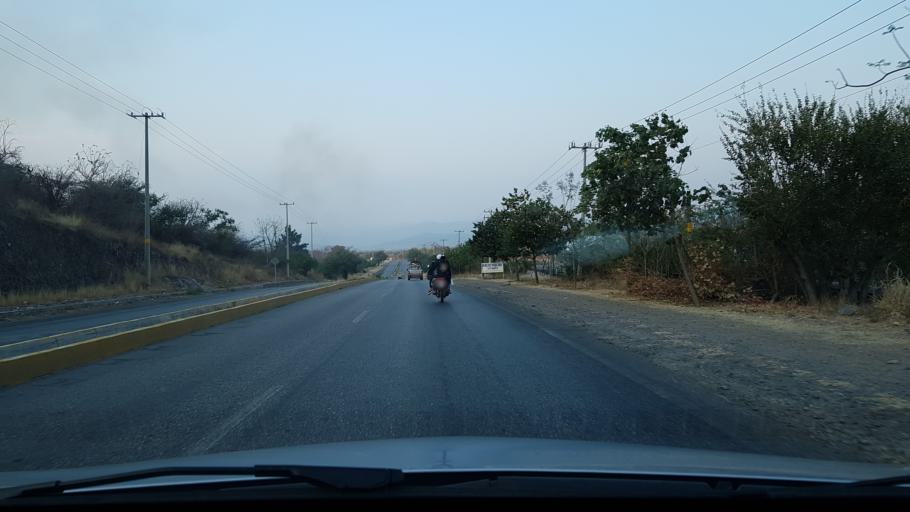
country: MX
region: Morelos
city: Jonacatepec de Leandro Valle
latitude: 18.6664
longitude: -98.8082
